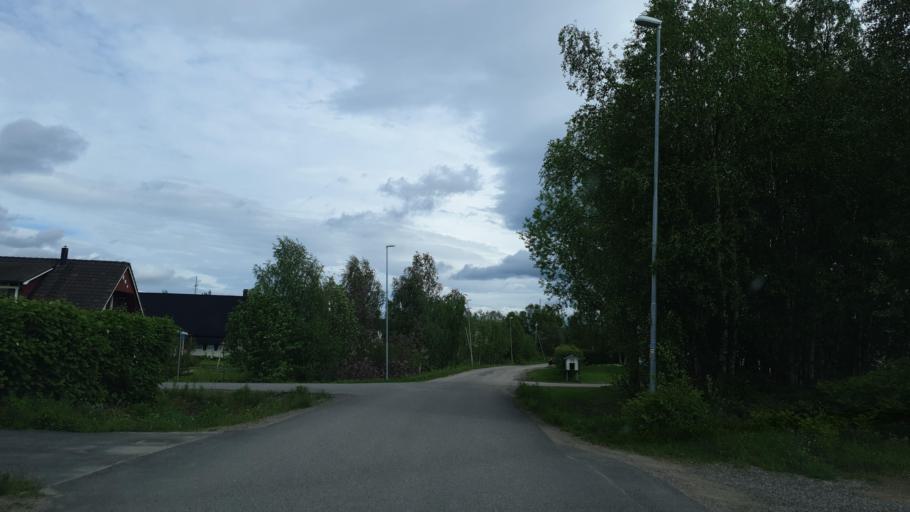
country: SE
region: Norrbotten
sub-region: Gallivare Kommun
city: Gaellivare
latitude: 67.1319
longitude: 20.6380
